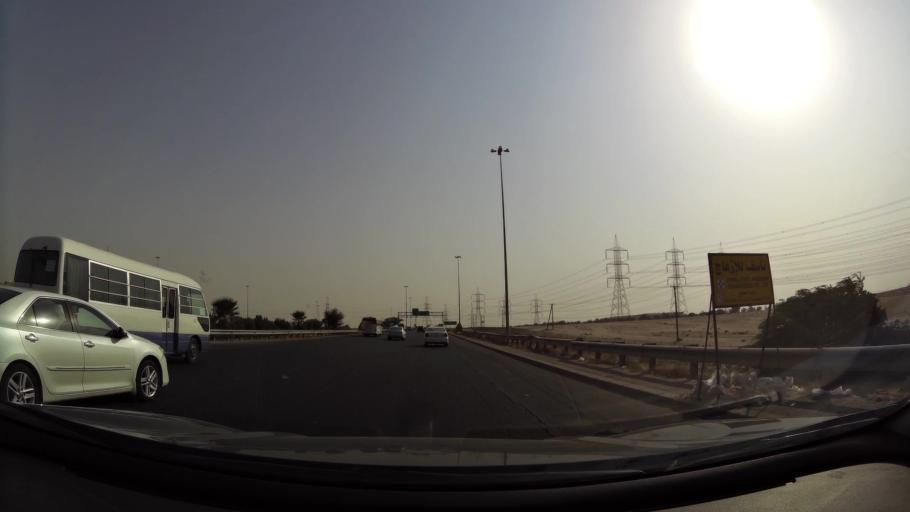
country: KW
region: Muhafazat al Jahra'
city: Al Jahra'
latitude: 29.3057
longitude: 47.7838
